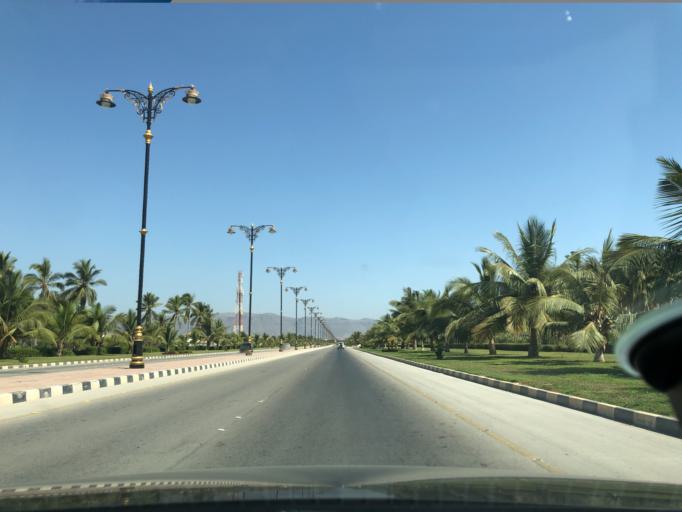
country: OM
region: Zufar
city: Salalah
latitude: 17.0415
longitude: 54.2035
